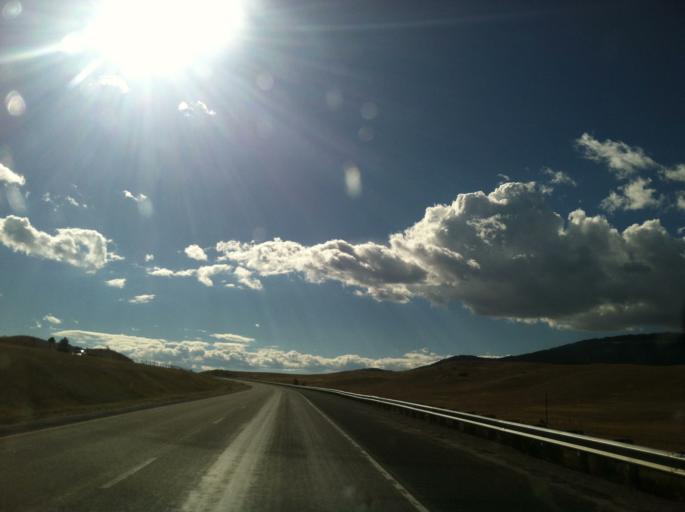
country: US
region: Montana
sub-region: Jefferson County
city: Whitehall
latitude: 45.8938
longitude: -111.8474
